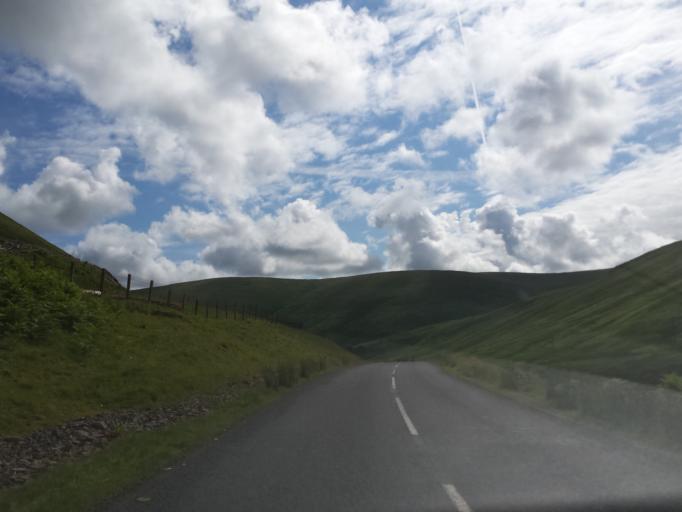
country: GB
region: Scotland
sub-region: The Scottish Borders
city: Peebles
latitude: 55.4406
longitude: -3.2449
